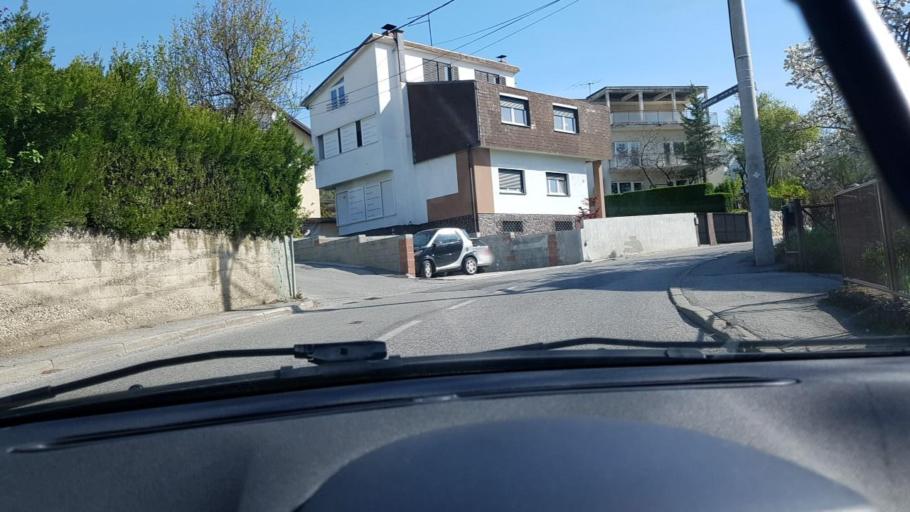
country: HR
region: Grad Zagreb
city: Zagreb
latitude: 45.8512
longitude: 15.9849
